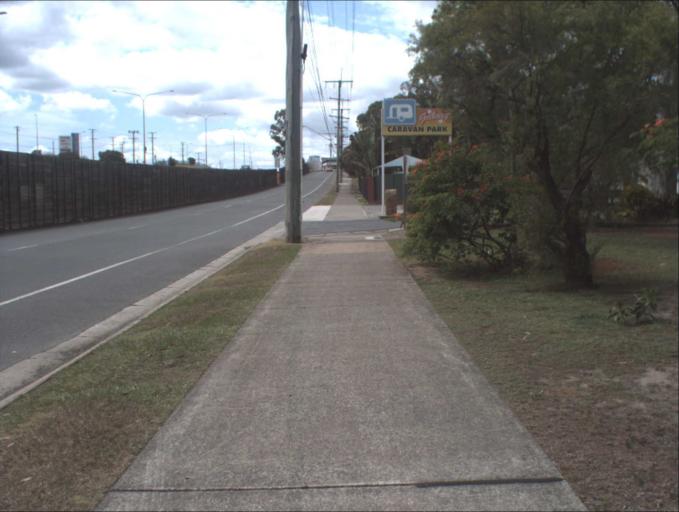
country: AU
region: Queensland
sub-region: Logan
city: Slacks Creek
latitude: -27.6596
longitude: 153.1678
